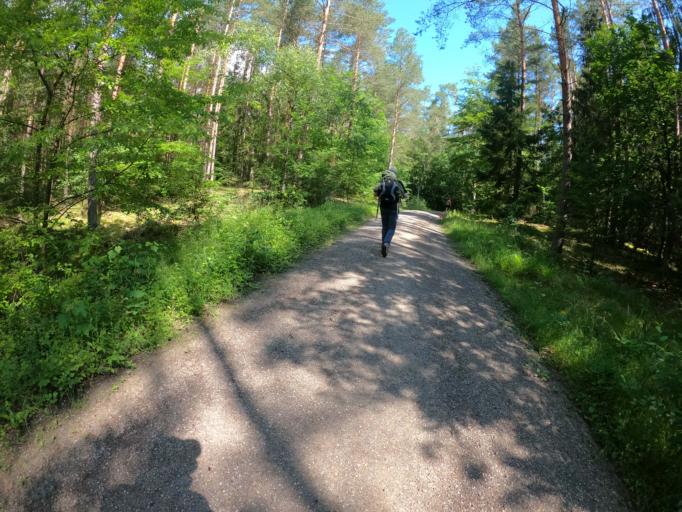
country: DE
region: Bavaria
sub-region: Upper Franconia
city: Strullendorf
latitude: 49.8847
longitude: 10.9545
